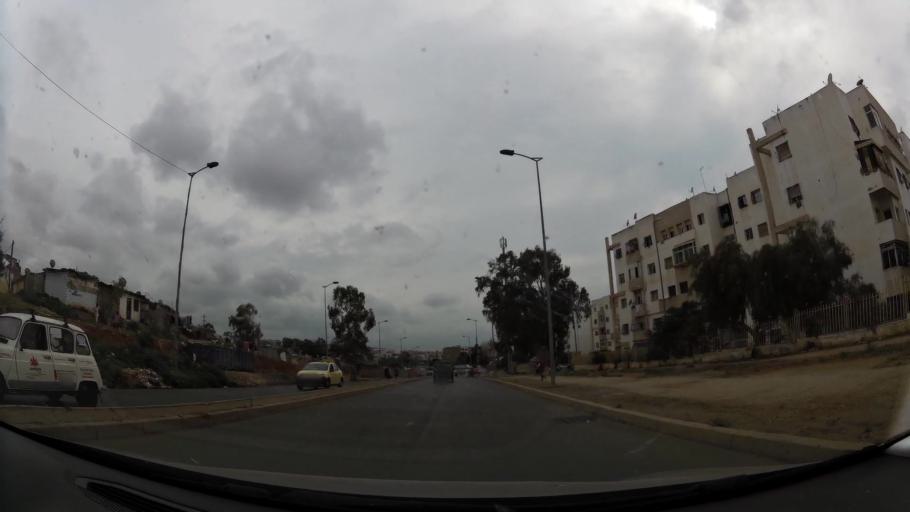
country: MA
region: Rabat-Sale-Zemmour-Zaer
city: Sale
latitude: 34.0397
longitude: -6.7982
